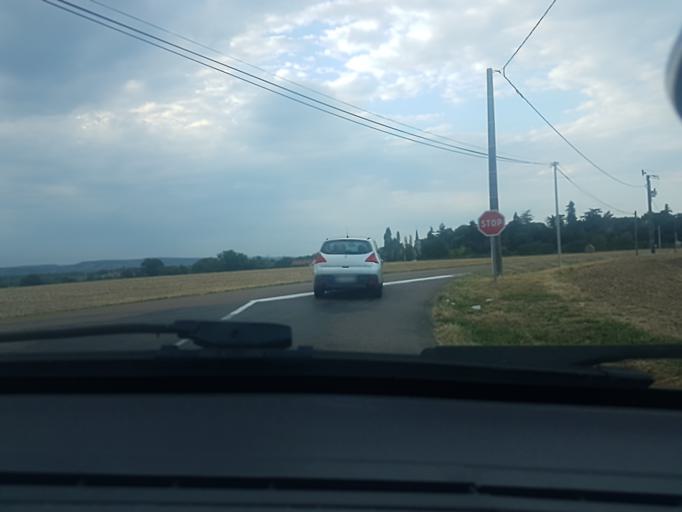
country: FR
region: Bourgogne
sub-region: Departement de Saone-et-Loire
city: Buxy
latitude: 46.7051
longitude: 4.7719
